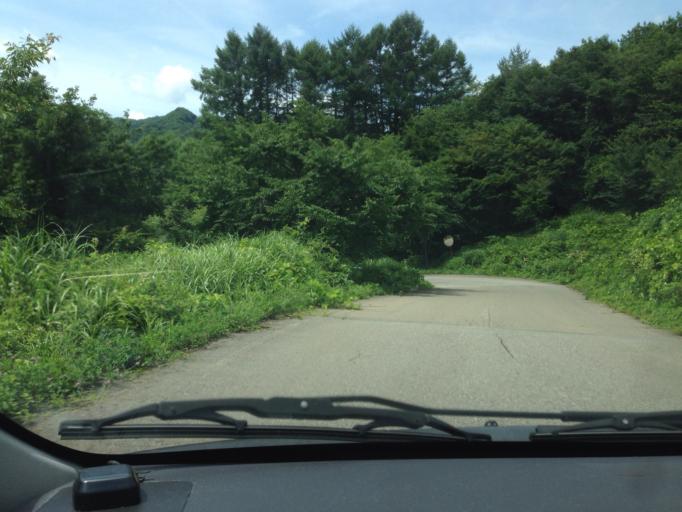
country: JP
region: Tochigi
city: Kuroiso
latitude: 37.2767
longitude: 139.8466
